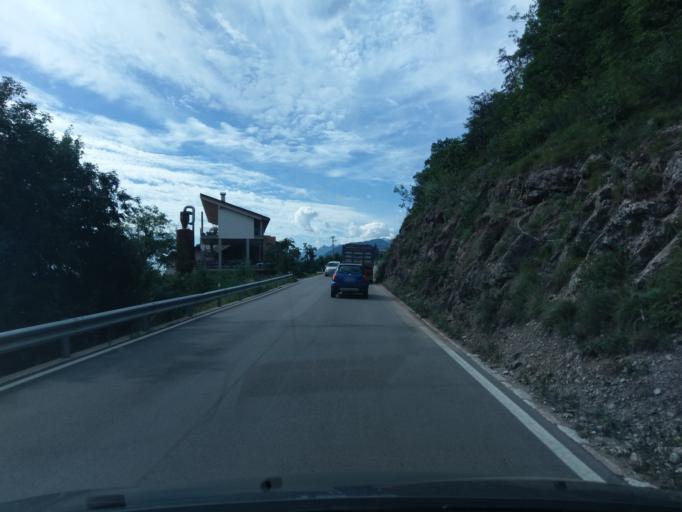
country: IT
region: Trentino-Alto Adige
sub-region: Provincia di Trento
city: Cagno
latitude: 46.3792
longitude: 11.0360
